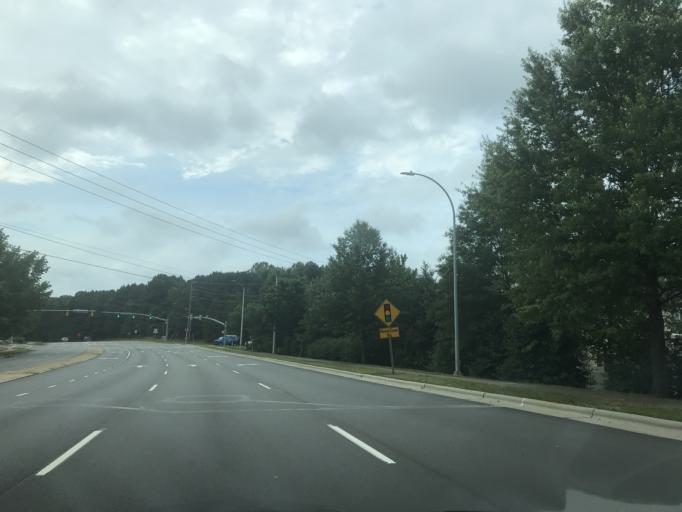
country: US
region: North Carolina
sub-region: Wake County
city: Cary
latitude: 35.8006
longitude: -78.7669
